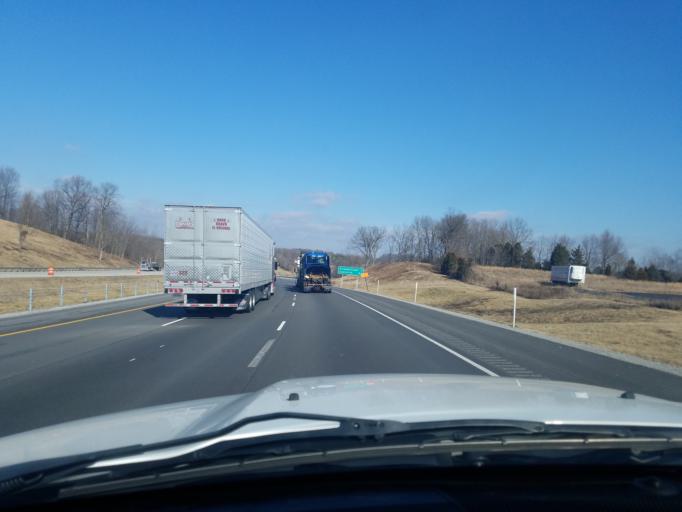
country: US
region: Kentucky
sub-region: Hardin County
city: Elizabethtown
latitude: 37.6830
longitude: -85.8427
